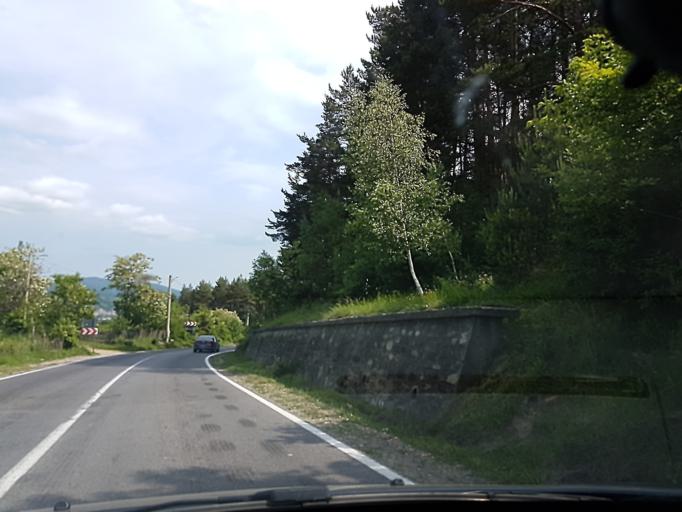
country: RO
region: Prahova
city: Maneciu
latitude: 45.3278
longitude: 25.9797
